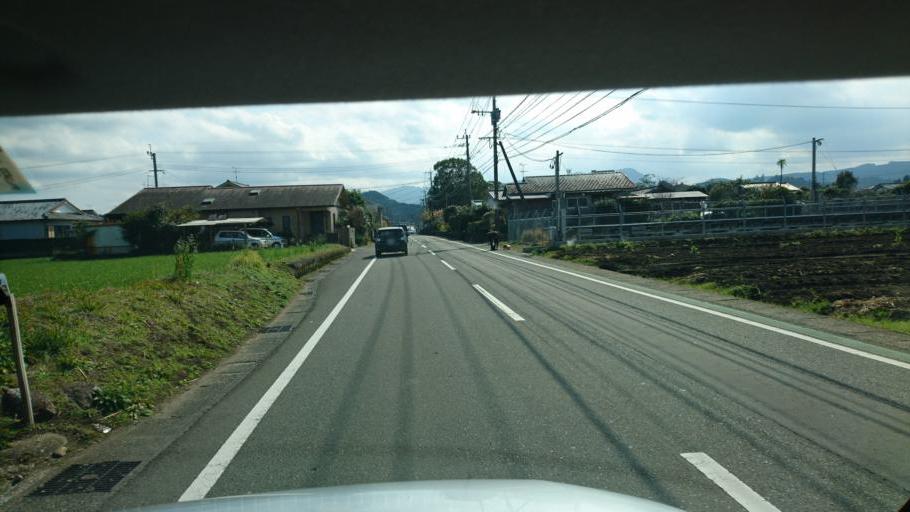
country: JP
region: Miyazaki
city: Miyazaki-shi
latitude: 31.8435
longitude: 131.3934
